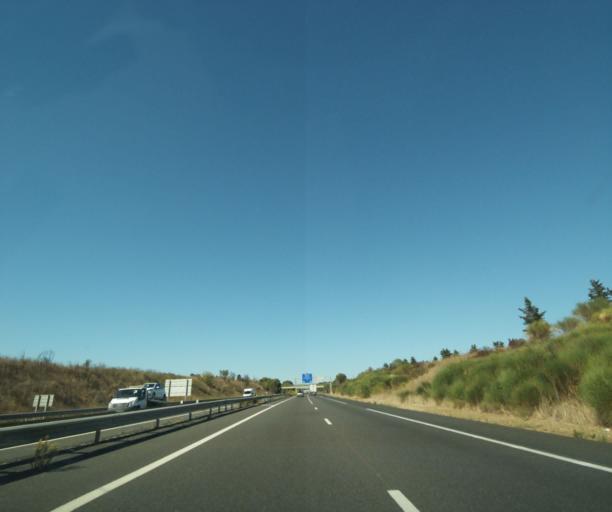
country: FR
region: Languedoc-Roussillon
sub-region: Departement du Gard
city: Garons
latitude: 43.7539
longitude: 4.4300
